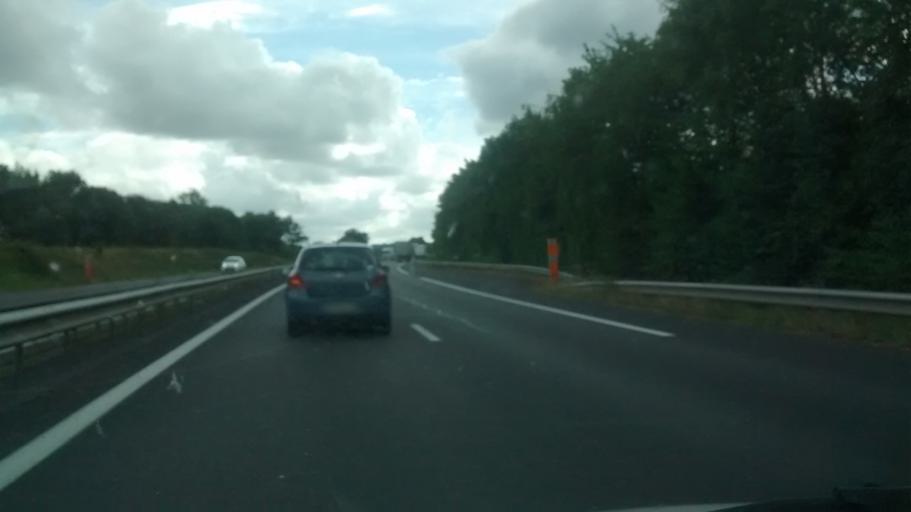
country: FR
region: Lower Normandy
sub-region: Departement du Calvados
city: Grainville-sur-Odon
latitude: 49.1194
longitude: -0.5750
